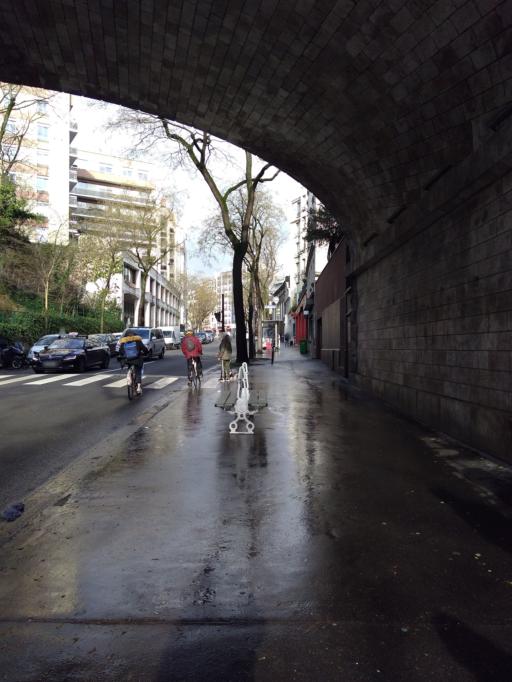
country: FR
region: Ile-de-France
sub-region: Departement de Seine-Saint-Denis
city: Bagnolet
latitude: 48.8617
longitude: 2.4003
